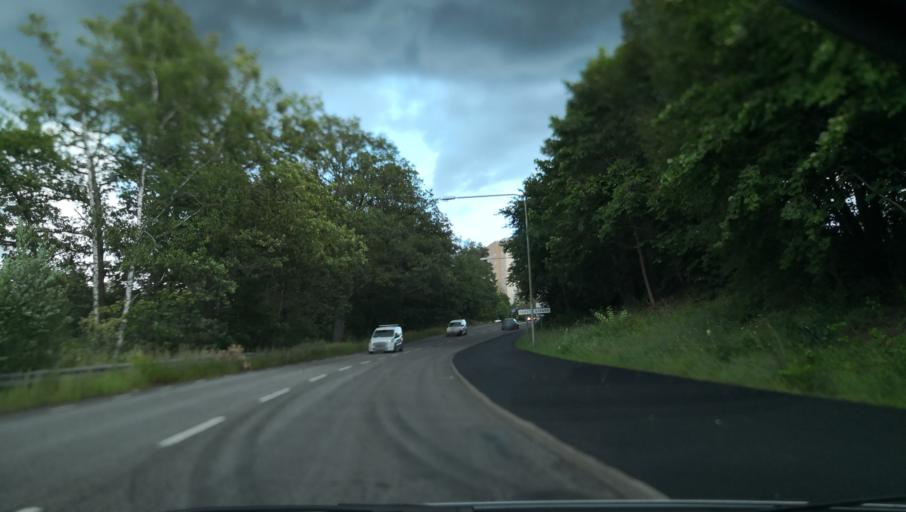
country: SE
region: Stockholm
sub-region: Stockholms Kommun
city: Arsta
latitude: 59.2392
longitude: 18.0901
